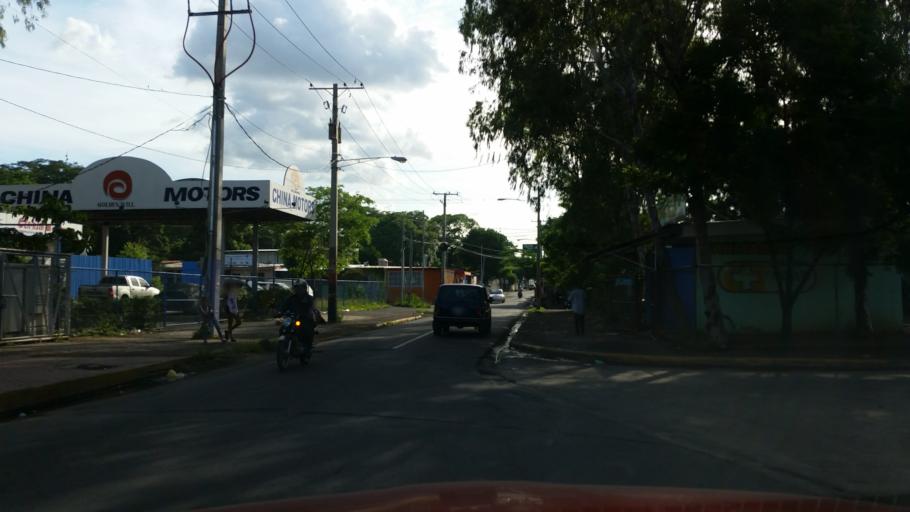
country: NI
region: Managua
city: Managua
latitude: 12.1486
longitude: -86.2747
